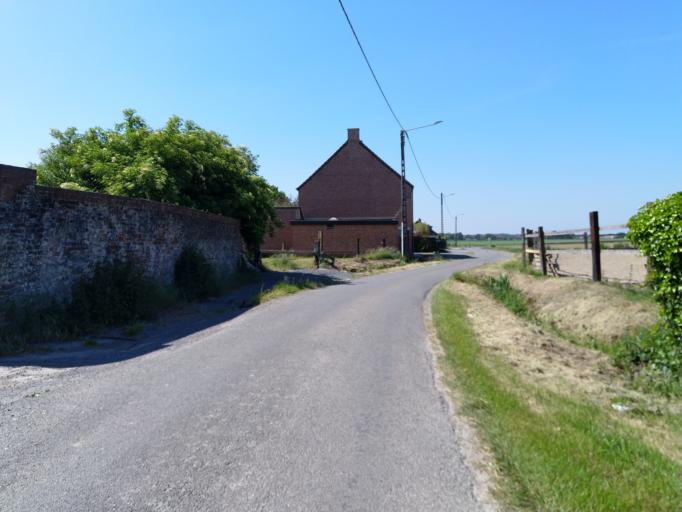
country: BE
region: Wallonia
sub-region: Province du Hainaut
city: Lens
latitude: 50.5370
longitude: 3.8625
